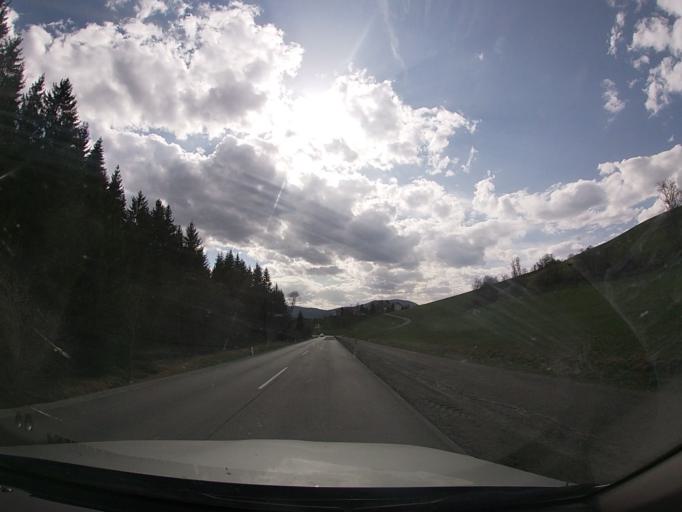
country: AT
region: Styria
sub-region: Politischer Bezirk Murau
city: Perchau am Sattel
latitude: 47.0938
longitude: 14.4454
